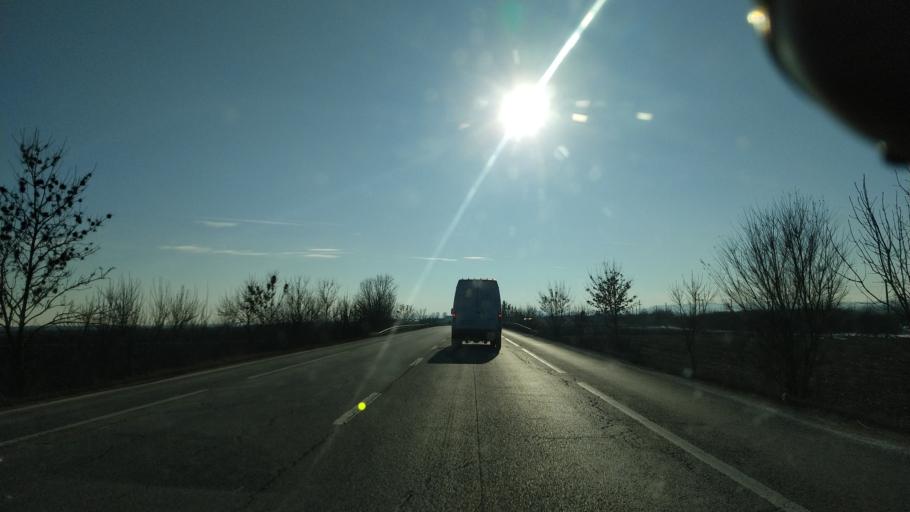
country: RO
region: Neamt
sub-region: Municipiul Roman
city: Roman
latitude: 46.8728
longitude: 26.8962
